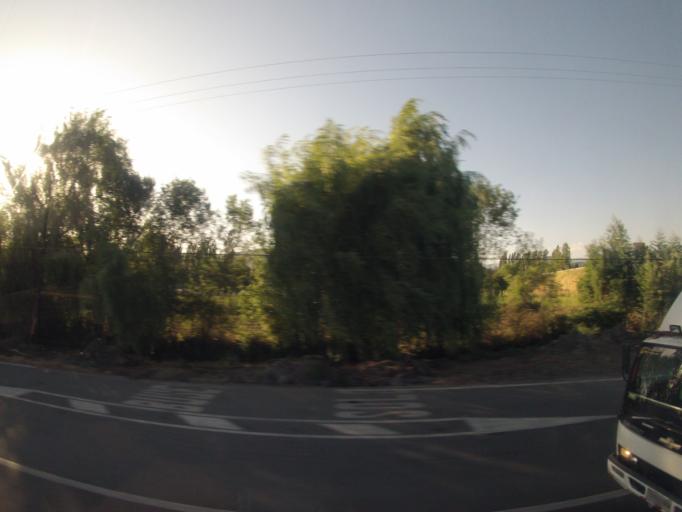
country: CL
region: O'Higgins
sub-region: Provincia de Colchagua
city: Chimbarongo
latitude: -34.6960
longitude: -71.0191
